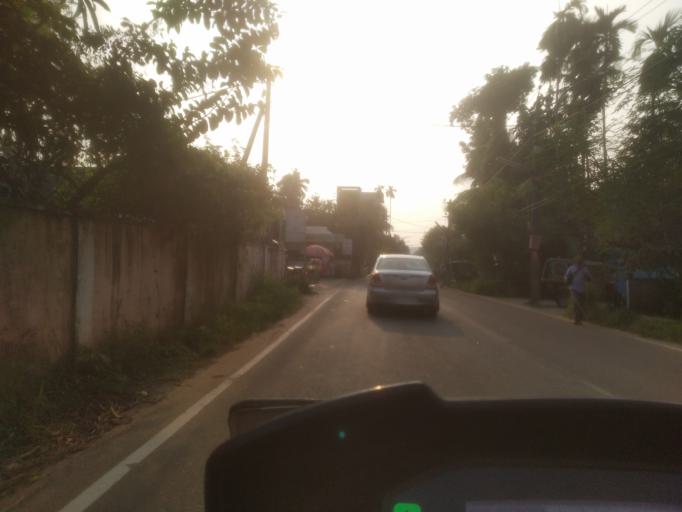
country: IN
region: Kerala
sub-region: Alappuzha
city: Arukutti
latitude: 9.9424
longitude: 76.3440
